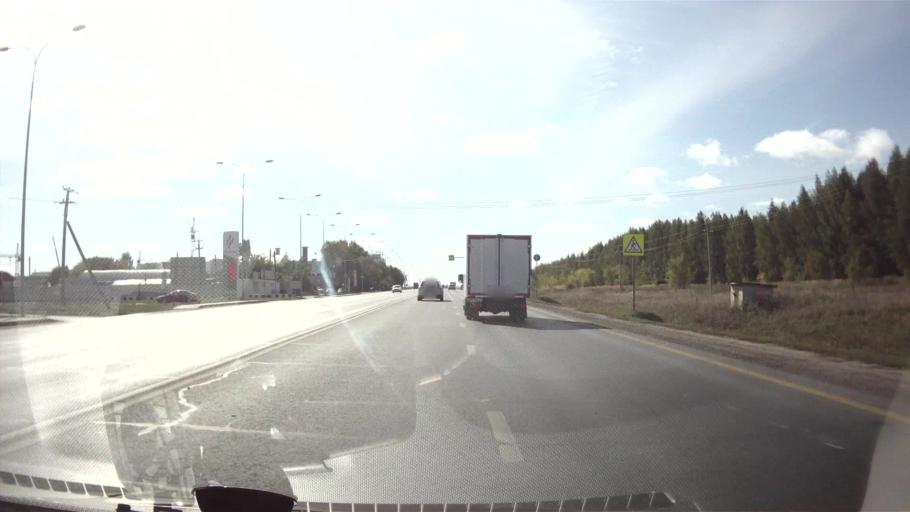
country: RU
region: Ulyanovsk
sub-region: Ulyanovskiy Rayon
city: Ulyanovsk
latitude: 54.2895
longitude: 48.2551
